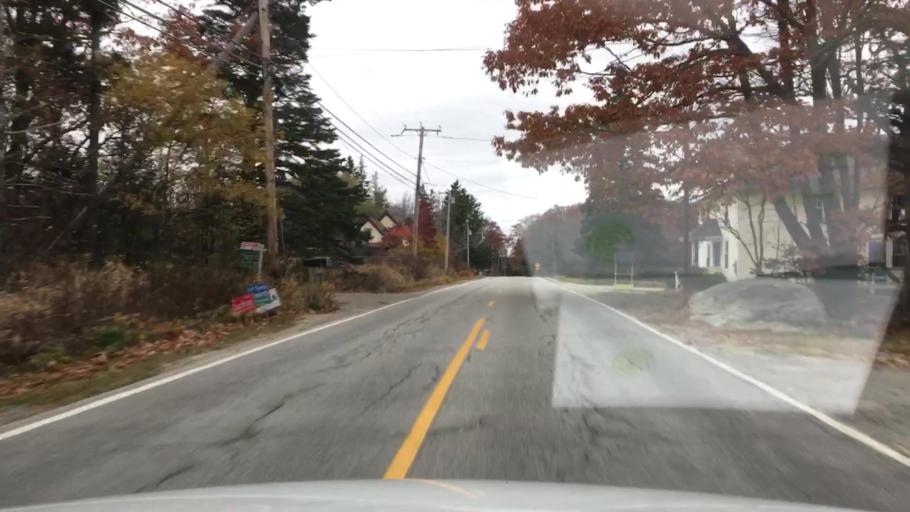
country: US
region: Maine
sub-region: Hancock County
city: Sedgwick
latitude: 44.3632
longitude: -68.5514
